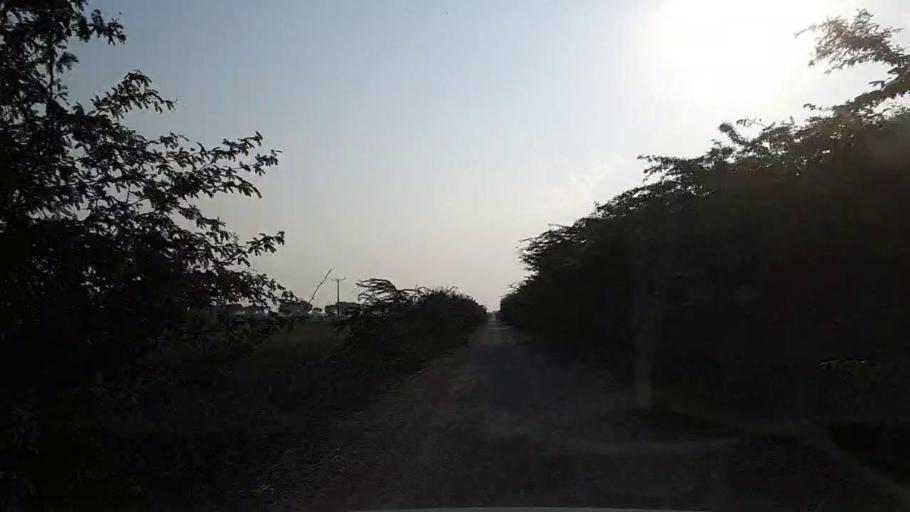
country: PK
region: Sindh
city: Mirpur Batoro
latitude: 24.7806
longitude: 68.2432
